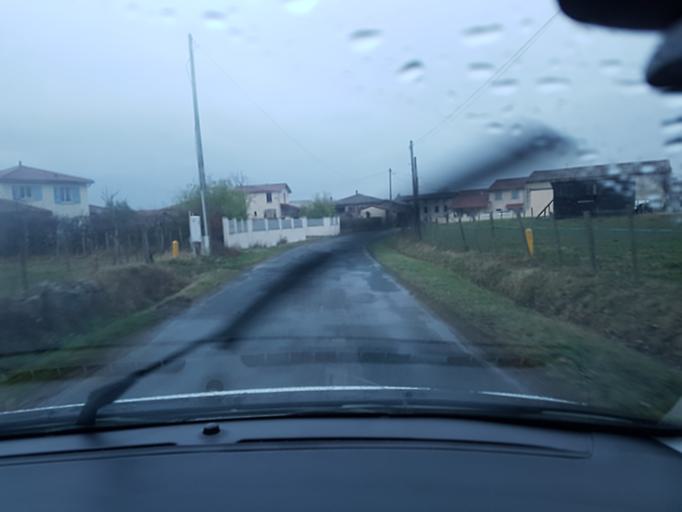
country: FR
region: Rhone-Alpes
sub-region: Departement du Rhone
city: Mornant
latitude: 45.6096
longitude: 4.6941
